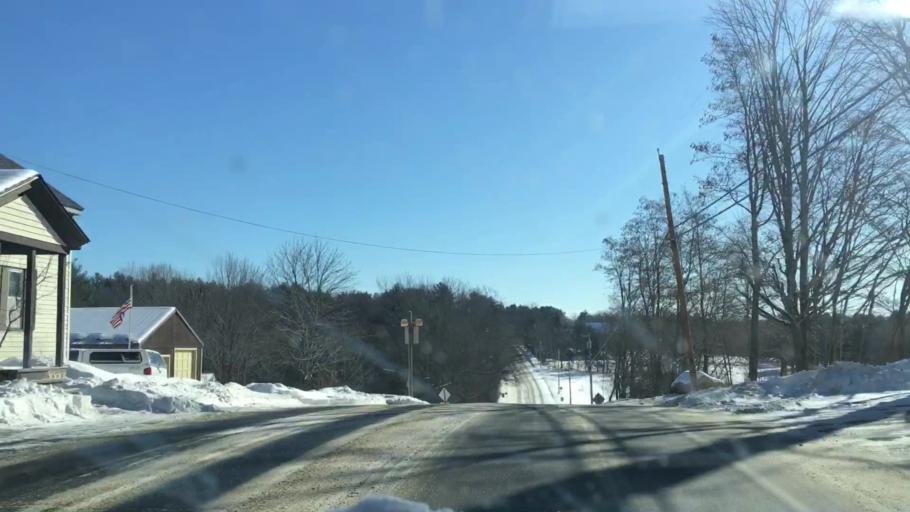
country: US
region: Maine
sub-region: Androscoggin County
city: Lisbon Falls
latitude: 43.9353
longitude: -70.0601
